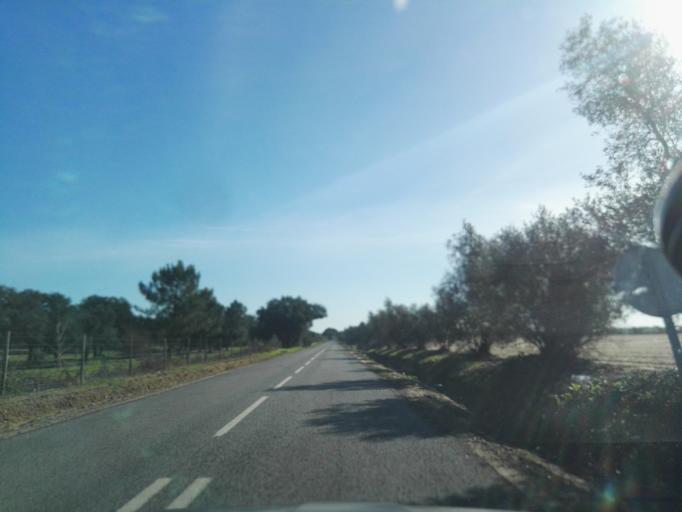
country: PT
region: Setubal
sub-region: Alcochete
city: Alcochete
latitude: 38.7327
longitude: -8.9242
